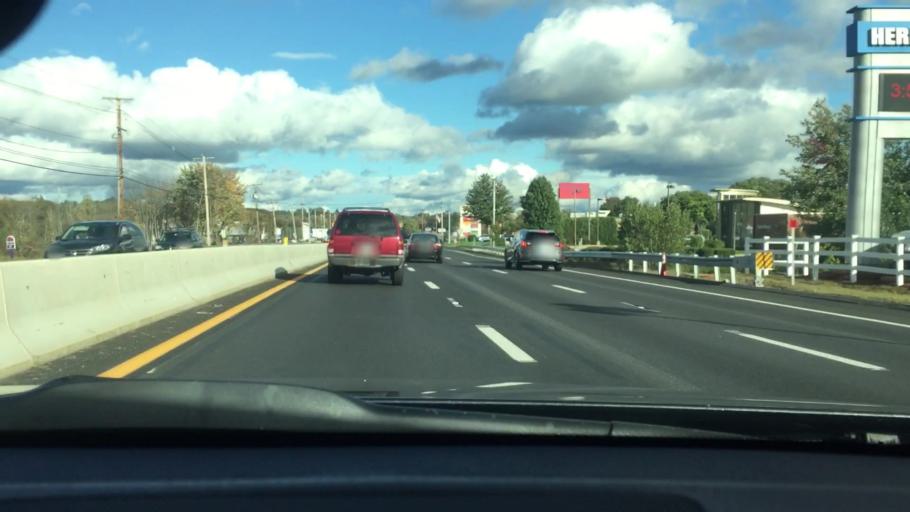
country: US
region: Massachusetts
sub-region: Worcester County
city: Westborough
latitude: 42.2828
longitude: -71.6495
